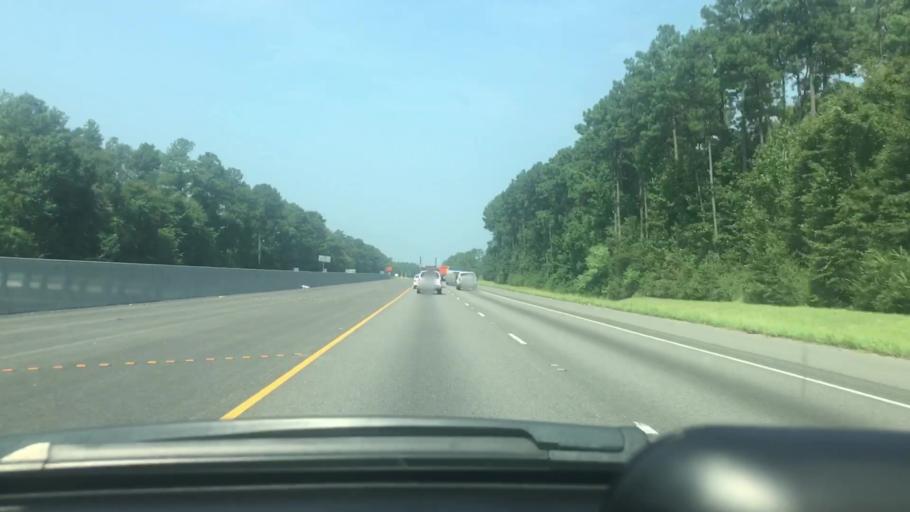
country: US
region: Louisiana
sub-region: Livingston Parish
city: Albany
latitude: 30.4747
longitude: -90.6558
